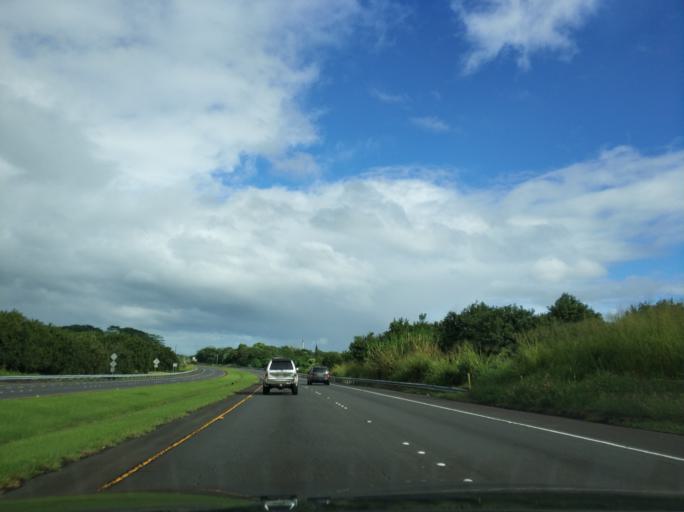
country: US
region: Hawaii
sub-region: Hawaii County
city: Kea'au
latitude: 19.6182
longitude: -155.0299
